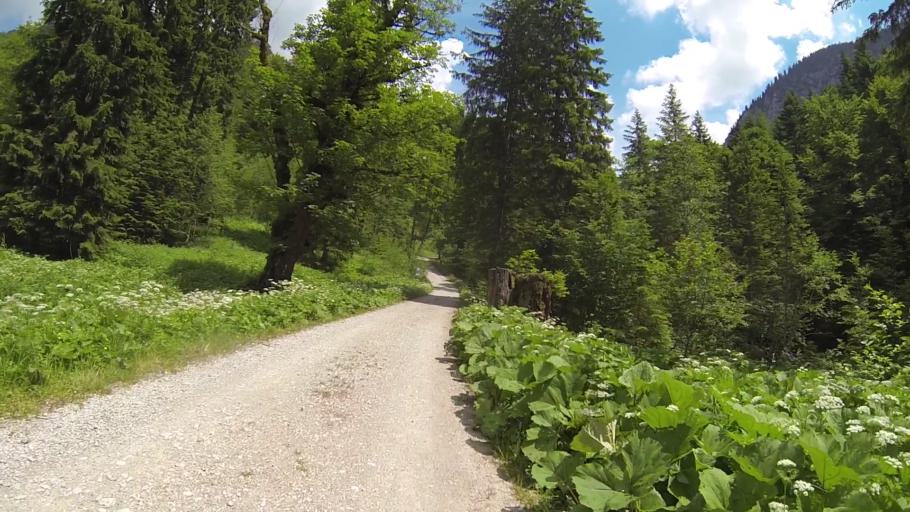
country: DE
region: Bavaria
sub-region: Swabia
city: Schwangau
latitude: 47.5348
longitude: 10.7798
